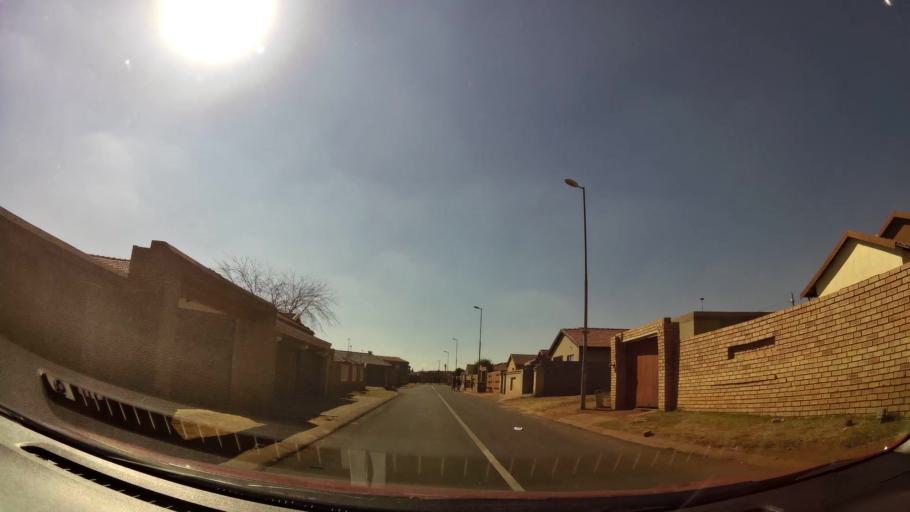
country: ZA
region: Gauteng
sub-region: City of Johannesburg Metropolitan Municipality
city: Soweto
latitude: -26.2378
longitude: 27.8196
